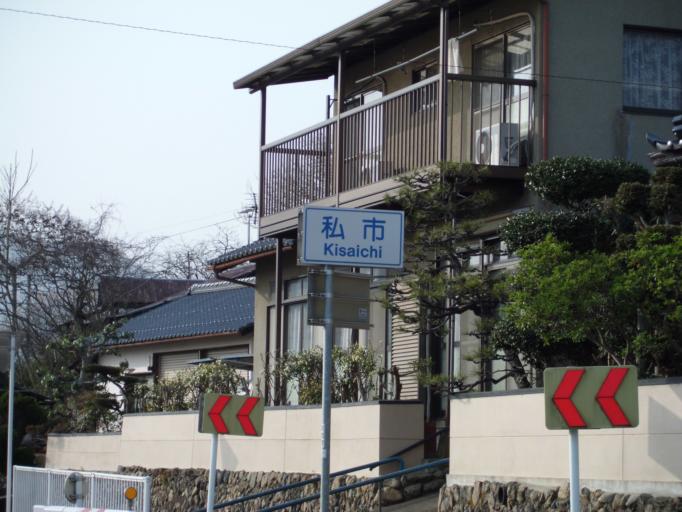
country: JP
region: Kyoto
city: Ayabe
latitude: 35.3145
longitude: 135.1908
